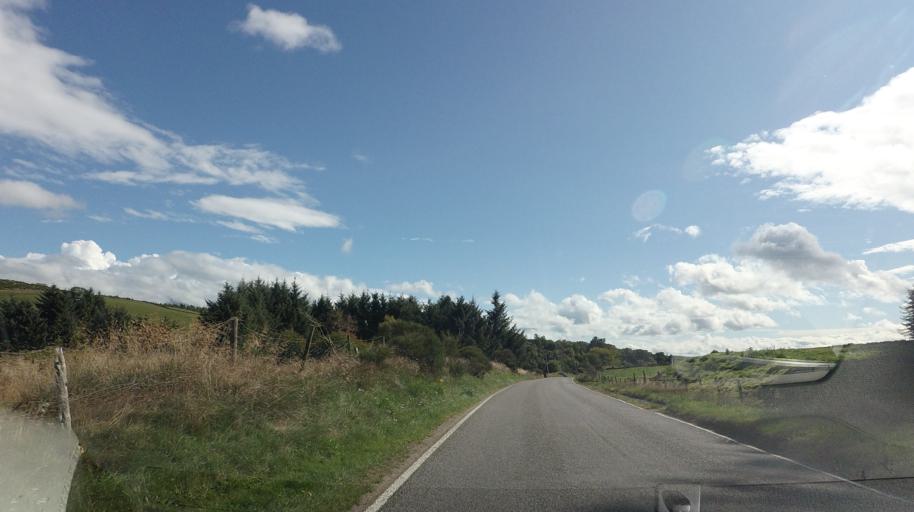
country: GB
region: Scotland
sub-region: Aberdeenshire
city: Torphins
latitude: 57.1351
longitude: -2.7005
